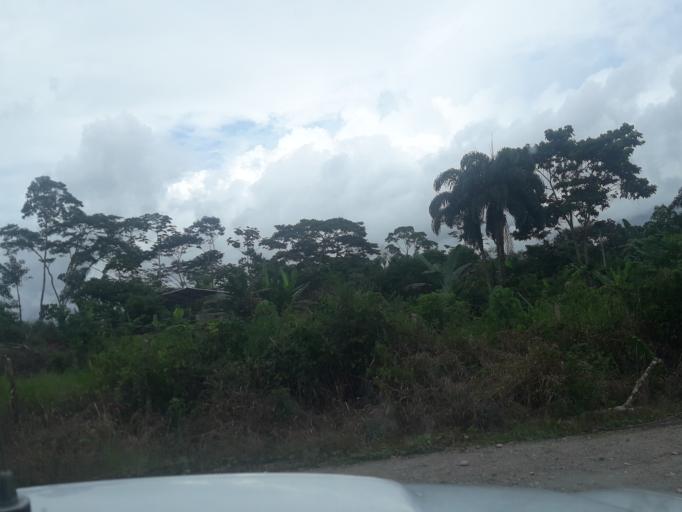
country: EC
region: Napo
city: Archidona
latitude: -0.9514
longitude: -77.8107
